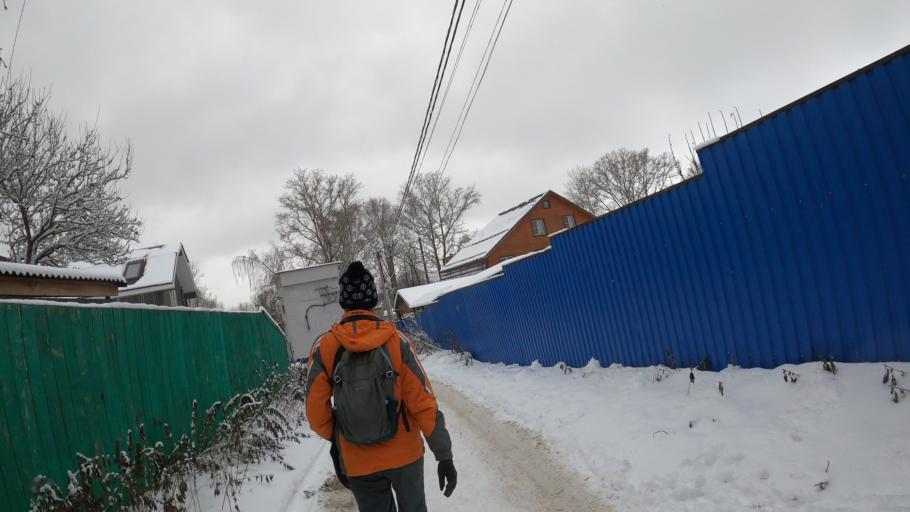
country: RU
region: Jaroslavl
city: Pereslavl'-Zalesskiy
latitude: 56.7449
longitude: 38.8626
